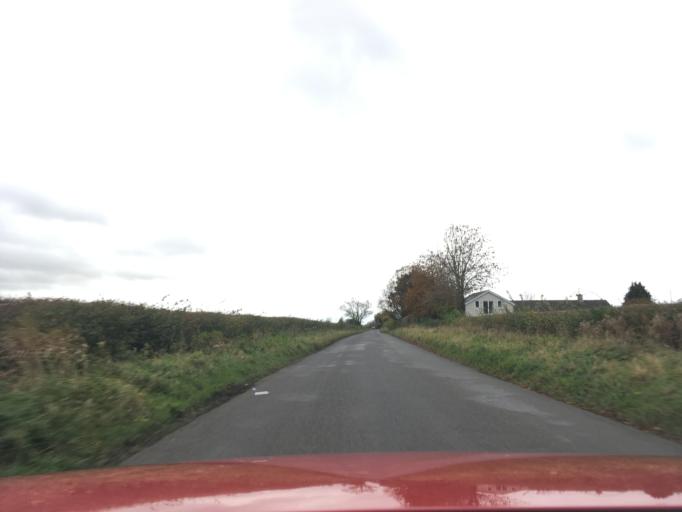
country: GB
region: England
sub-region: Somerset
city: Yeovil
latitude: 51.0067
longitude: -2.5944
